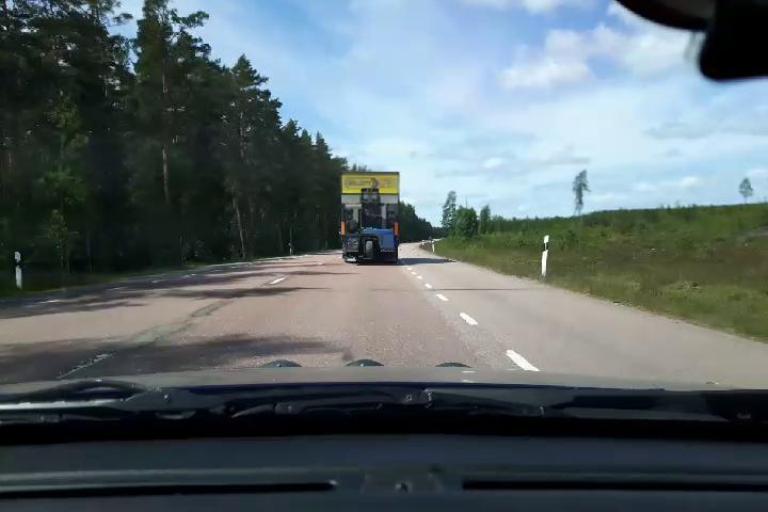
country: SE
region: Uppsala
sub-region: Osthammars Kommun
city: Bjorklinge
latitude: 60.1135
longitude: 17.5237
